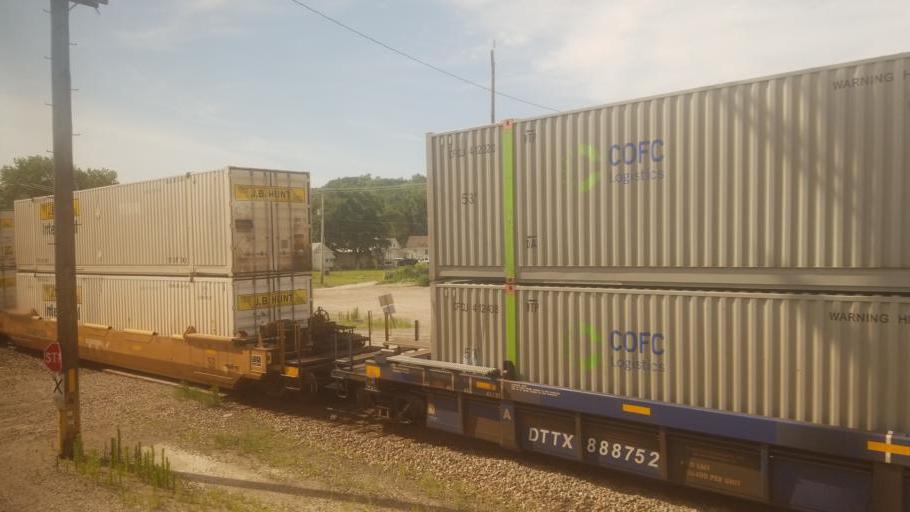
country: US
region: Kansas
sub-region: Johnson County
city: Mission
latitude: 39.0774
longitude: -94.6631
